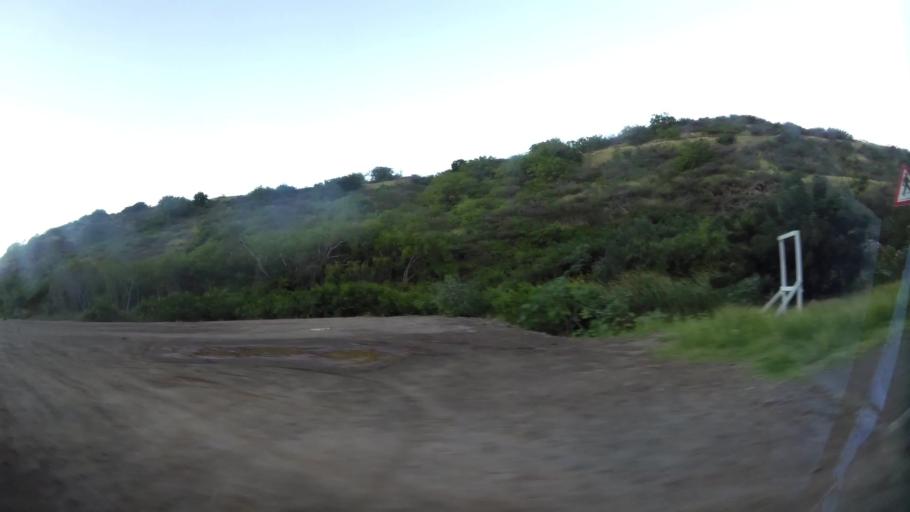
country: MS
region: Saint Peter
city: Brades
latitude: 16.7974
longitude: -62.2051
